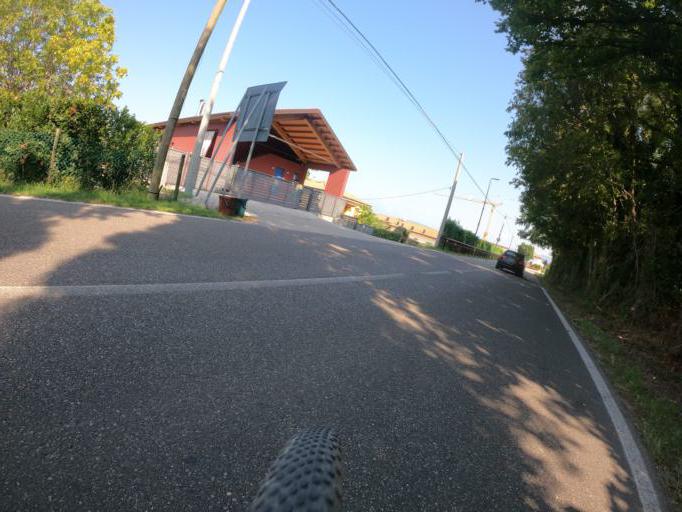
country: IT
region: Veneto
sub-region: Provincia di Verona
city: Lazise
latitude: 45.5099
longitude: 10.7439
